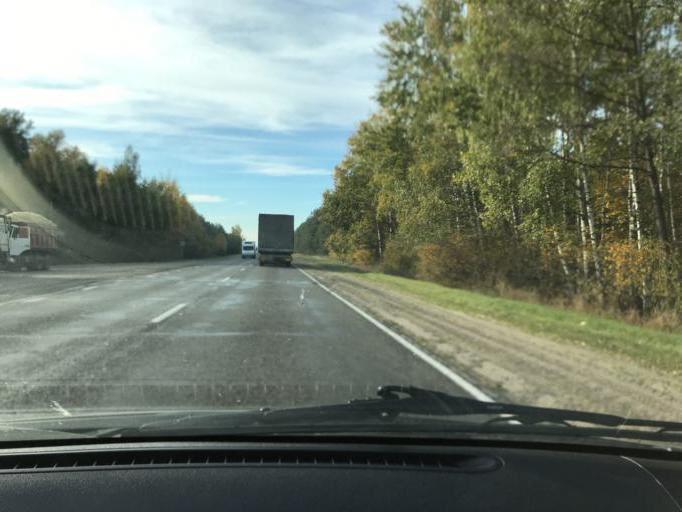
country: BY
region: Brest
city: Horad Pinsk
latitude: 52.1518
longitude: 25.8379
